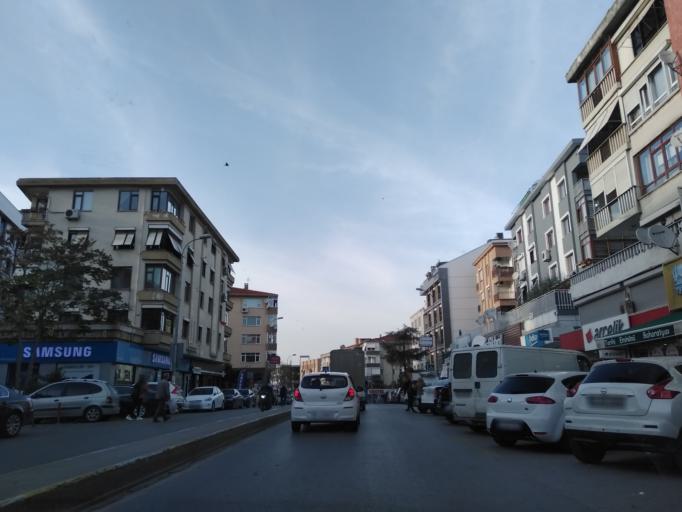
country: TR
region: Istanbul
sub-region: Atasehir
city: Atasehir
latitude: 40.9481
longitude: 29.1066
